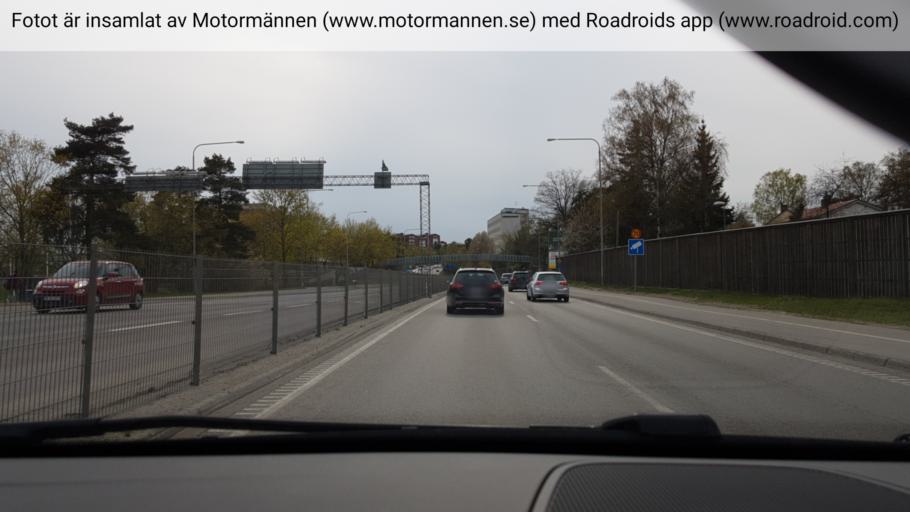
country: SE
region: Stockholm
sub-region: Huddinge Kommun
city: Huddinge
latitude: 59.2454
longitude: 17.9995
